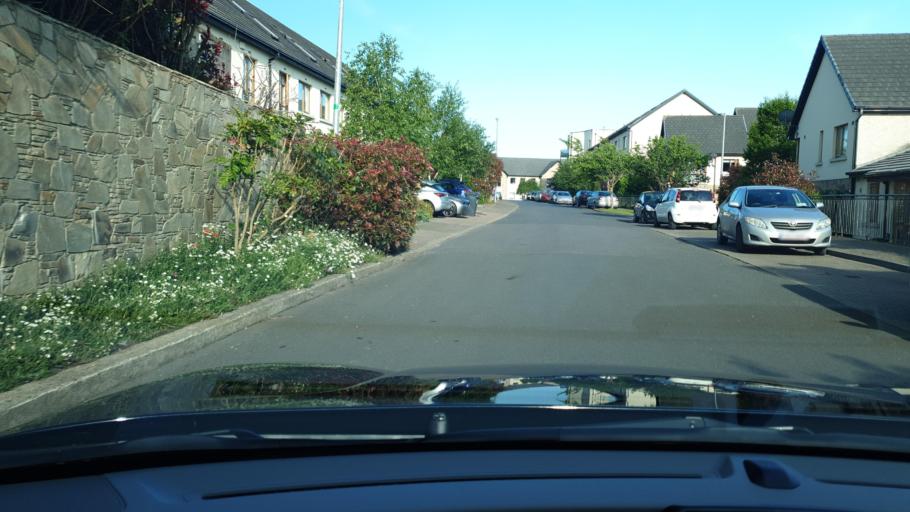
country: IE
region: Leinster
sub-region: An Mhi
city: Ashbourne
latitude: 53.5137
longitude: -6.4134
